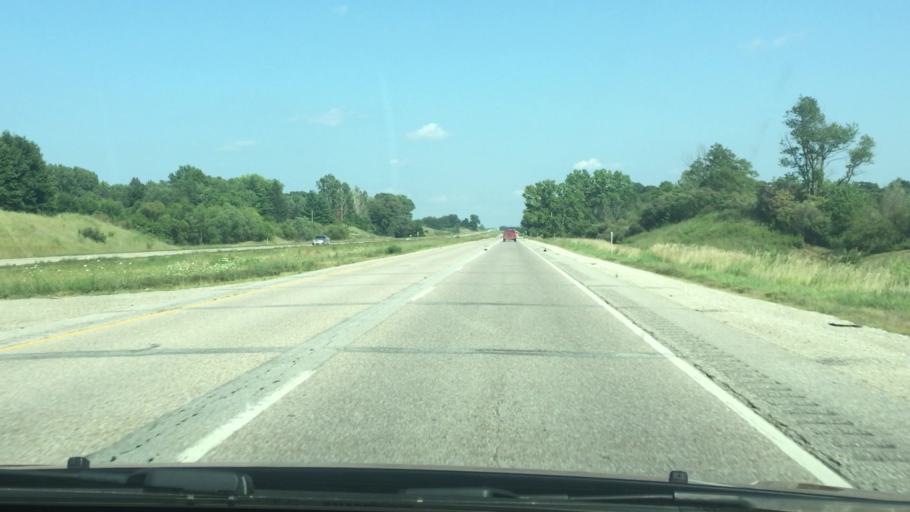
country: US
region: Iowa
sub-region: Scott County
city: Blue Grass
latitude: 41.5159
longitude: -90.8309
